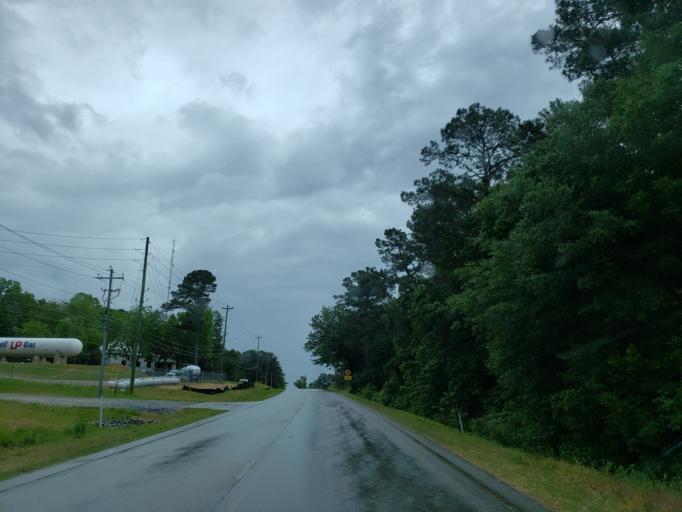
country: US
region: Georgia
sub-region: Haralson County
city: Buchanan
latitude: 33.7938
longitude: -85.1850
